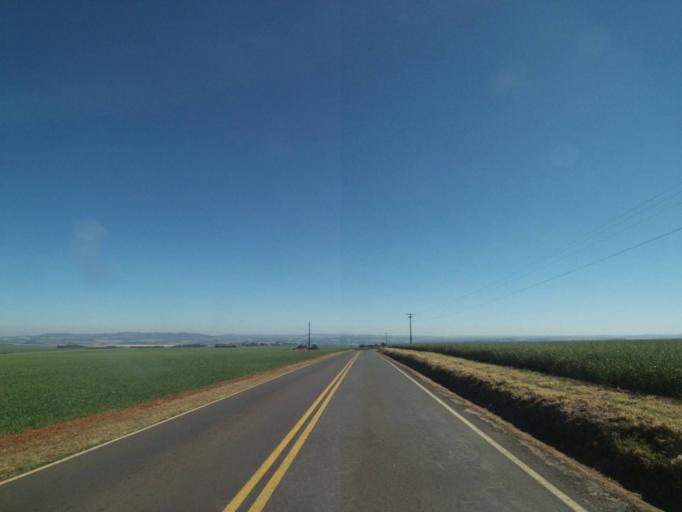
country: BR
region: Parana
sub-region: Tibagi
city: Tibagi
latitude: -24.5199
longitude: -50.3325
